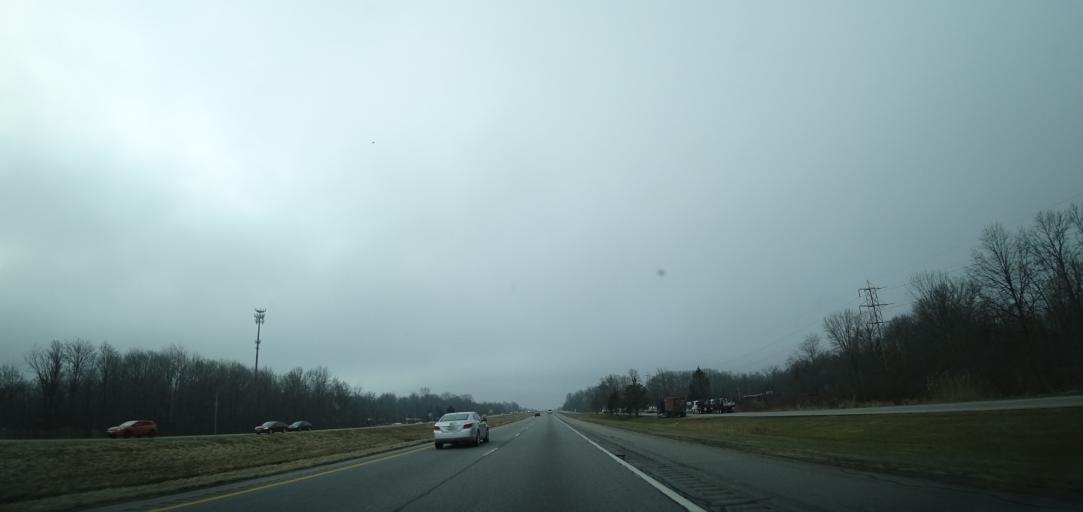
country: US
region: Ohio
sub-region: Summit County
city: Richfield
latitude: 41.1972
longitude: -81.6260
